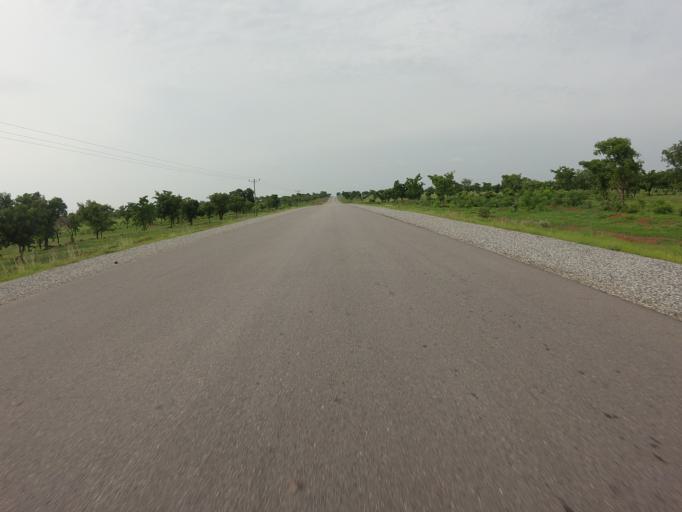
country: GH
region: Northern
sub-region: Yendi
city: Yendi
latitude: 9.8199
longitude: -0.1182
